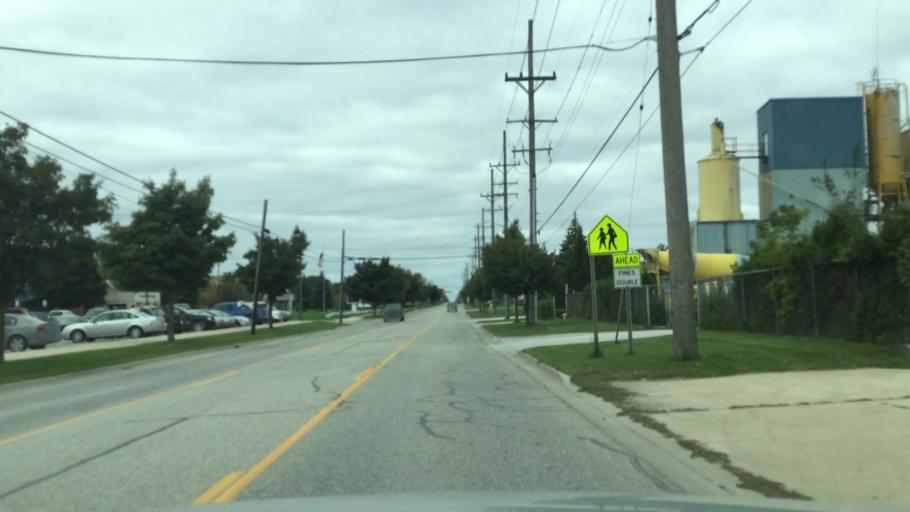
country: US
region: Michigan
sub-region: Macomb County
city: Richmond
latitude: 42.8092
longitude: -82.7581
